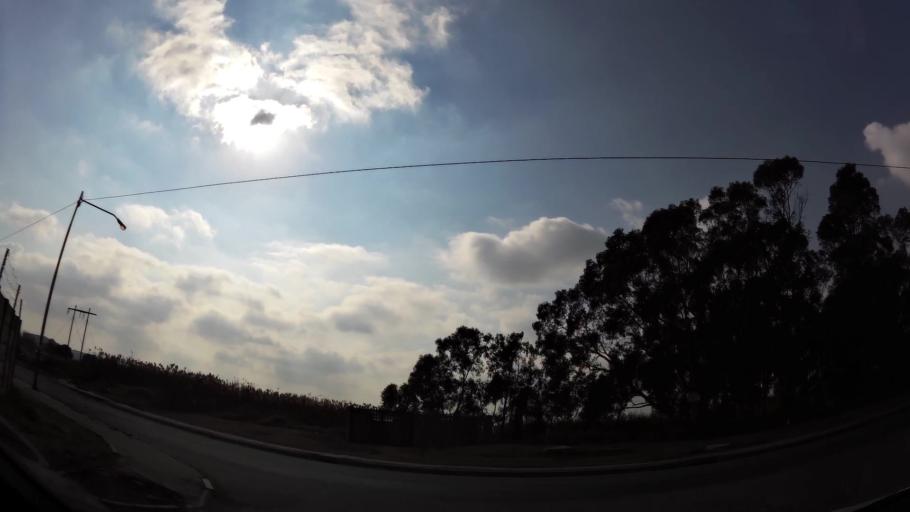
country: ZA
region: Gauteng
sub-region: City of Johannesburg Metropolitan Municipality
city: Modderfontein
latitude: -26.1554
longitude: 28.2045
